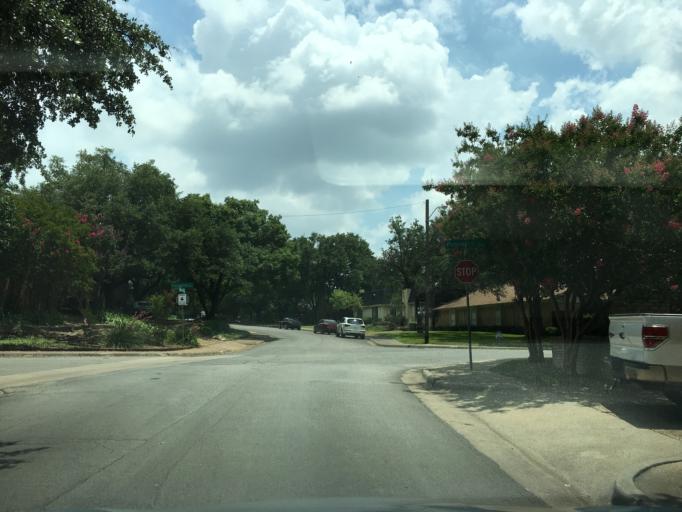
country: US
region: Texas
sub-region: Dallas County
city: University Park
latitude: 32.8919
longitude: -96.7821
